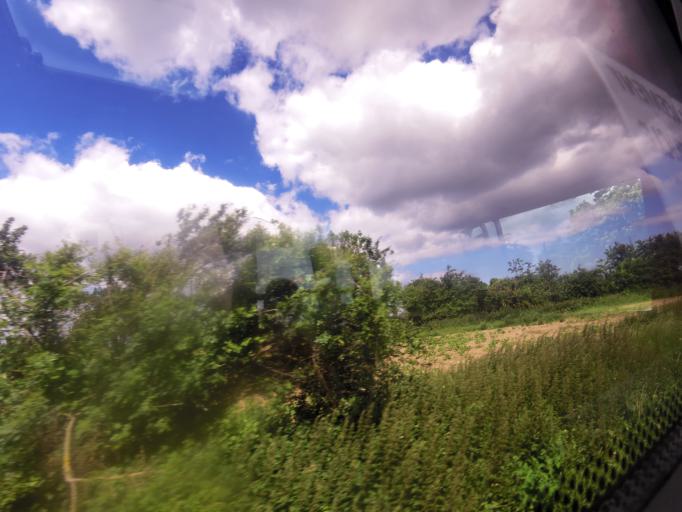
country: GB
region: England
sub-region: Norfolk
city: Cromer
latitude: 52.8772
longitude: 1.2926
